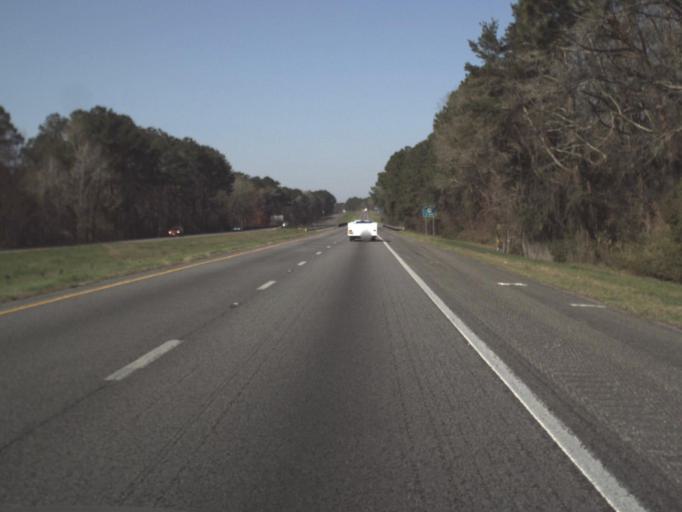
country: US
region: Florida
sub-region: Jefferson County
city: Monticello
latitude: 30.4896
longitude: -84.0013
